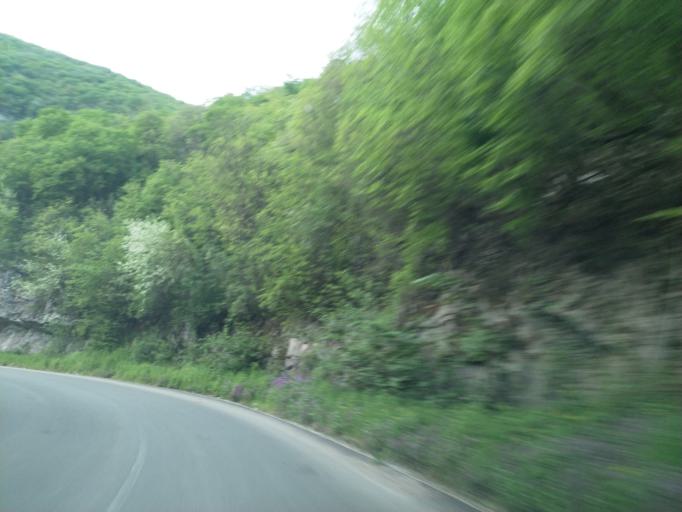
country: RS
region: Central Serbia
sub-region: Pomoravski Okrug
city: Despotovac
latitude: 43.9715
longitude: 21.5249
